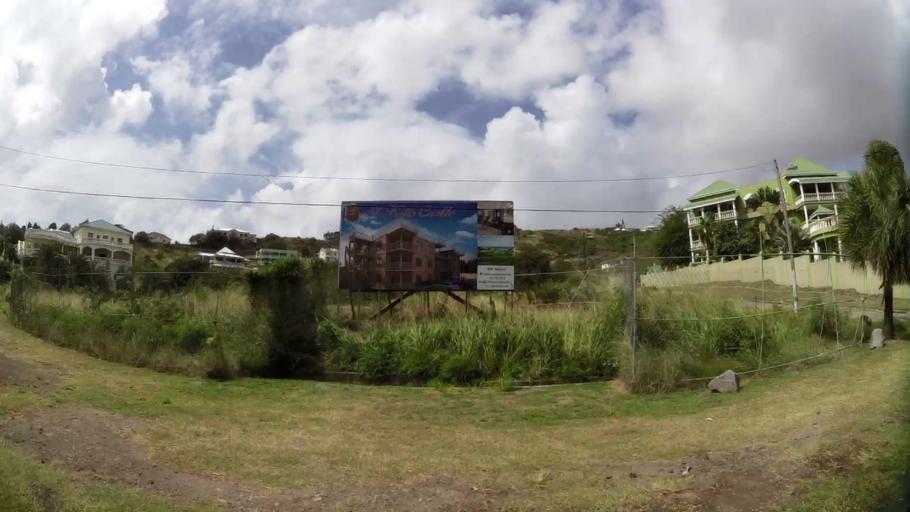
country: KN
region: Saint George Basseterre
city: Basseterre
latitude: 17.2859
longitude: -62.6925
